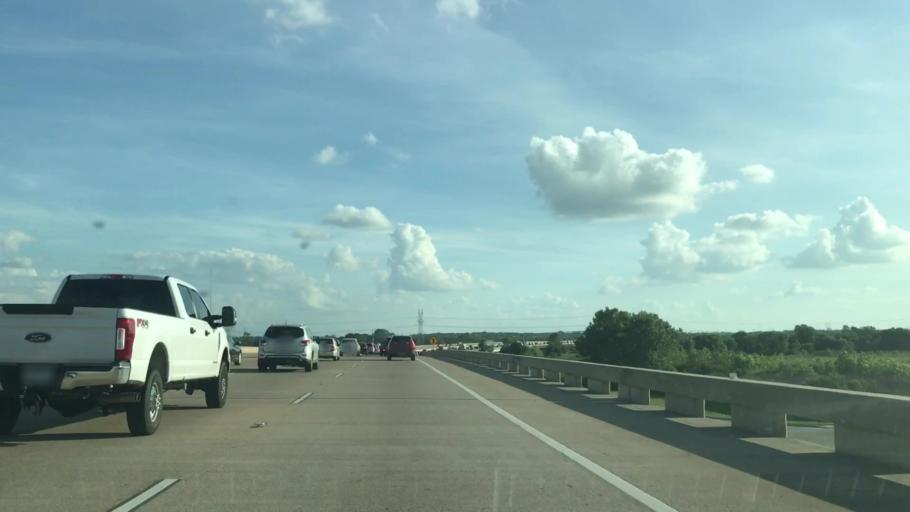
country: US
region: Texas
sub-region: Dallas County
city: Grand Prairie
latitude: 32.7899
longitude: -97.0170
